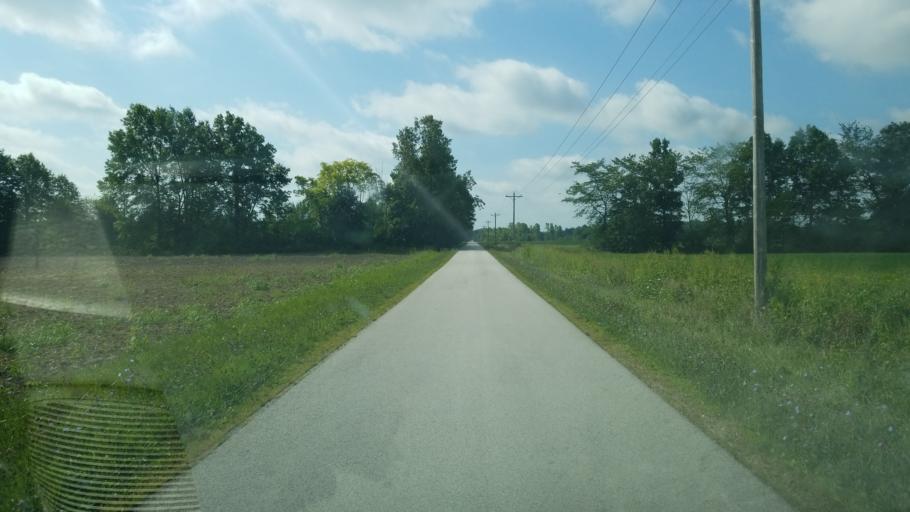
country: US
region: Ohio
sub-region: Wyandot County
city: Upper Sandusky
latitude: 40.7247
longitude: -83.3624
